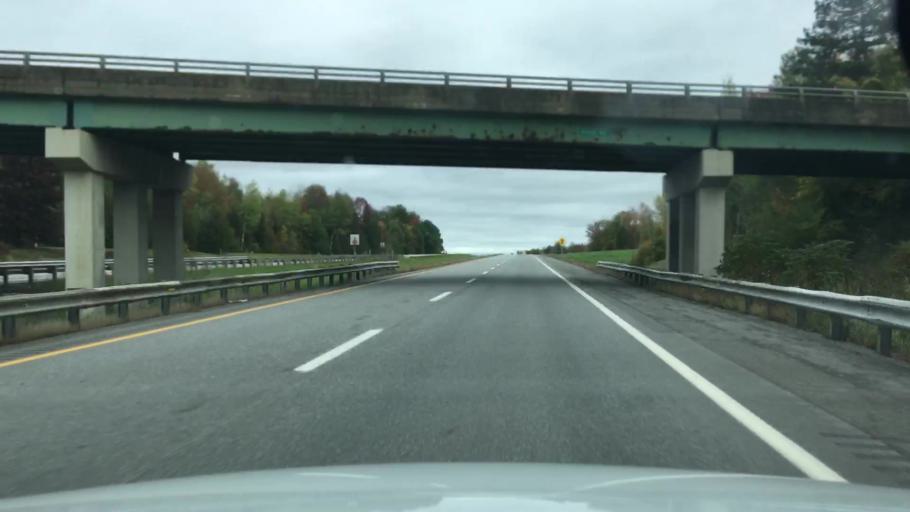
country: US
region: Maine
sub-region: Penobscot County
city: Newport
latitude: 44.8186
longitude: -69.2599
